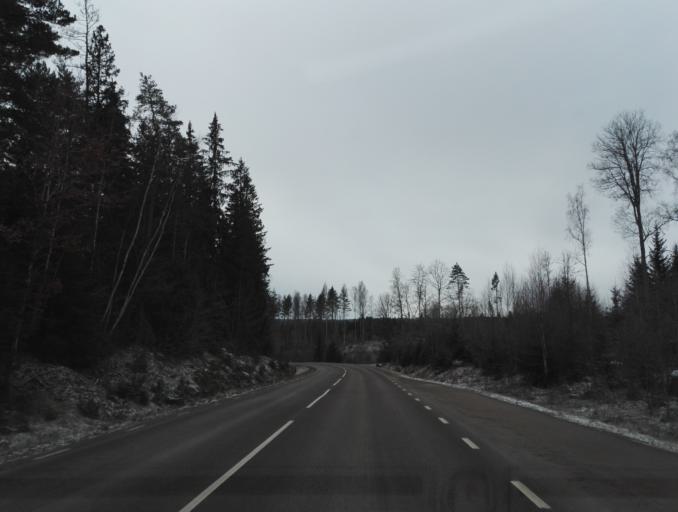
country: SE
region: Kalmar
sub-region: Hultsfreds Kommun
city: Virserum
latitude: 57.3617
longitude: 15.6125
